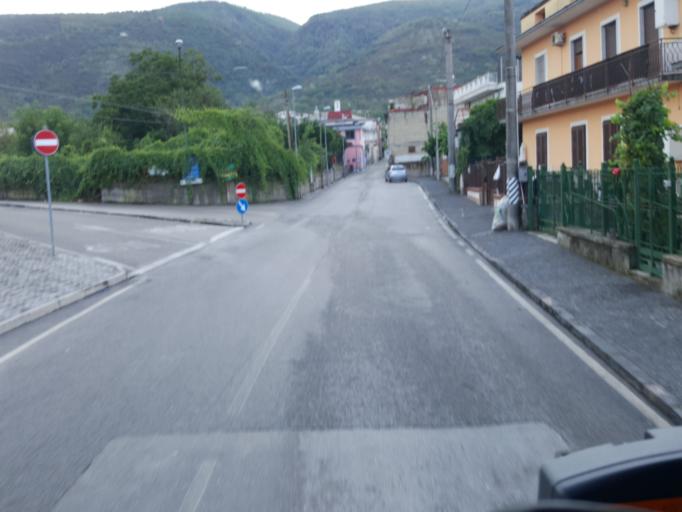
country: IT
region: Campania
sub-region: Provincia di Napoli
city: Carbonara di Nola
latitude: 40.8792
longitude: 14.5768
